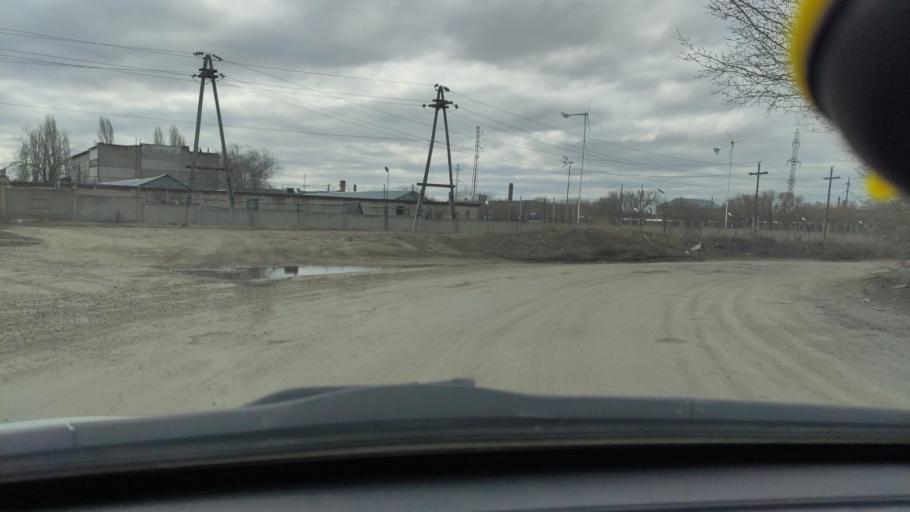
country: RU
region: Samara
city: Tol'yatti
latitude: 53.5266
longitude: 49.4601
